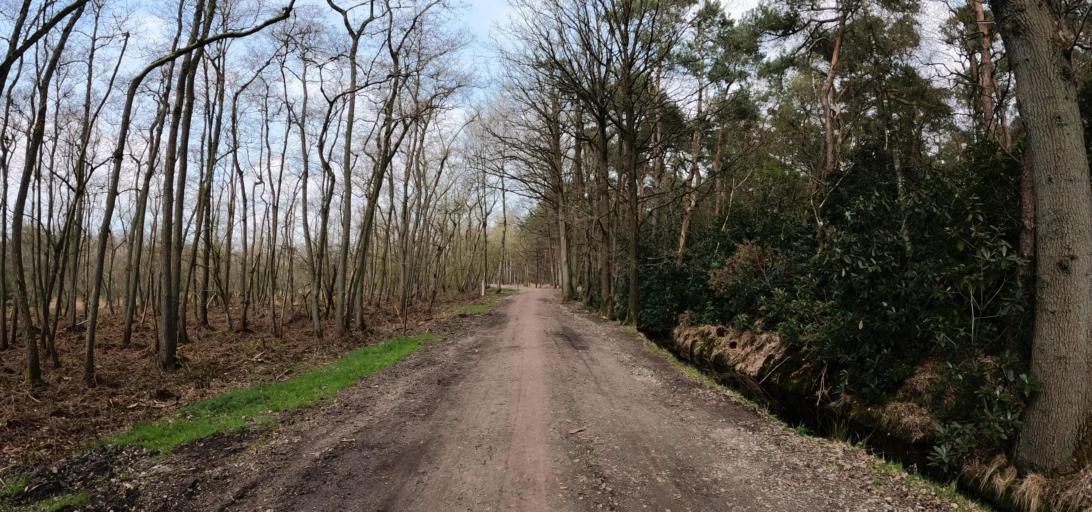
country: BE
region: Flanders
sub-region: Provincie Antwerpen
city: Kalmthout
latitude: 51.4205
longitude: 4.4401
